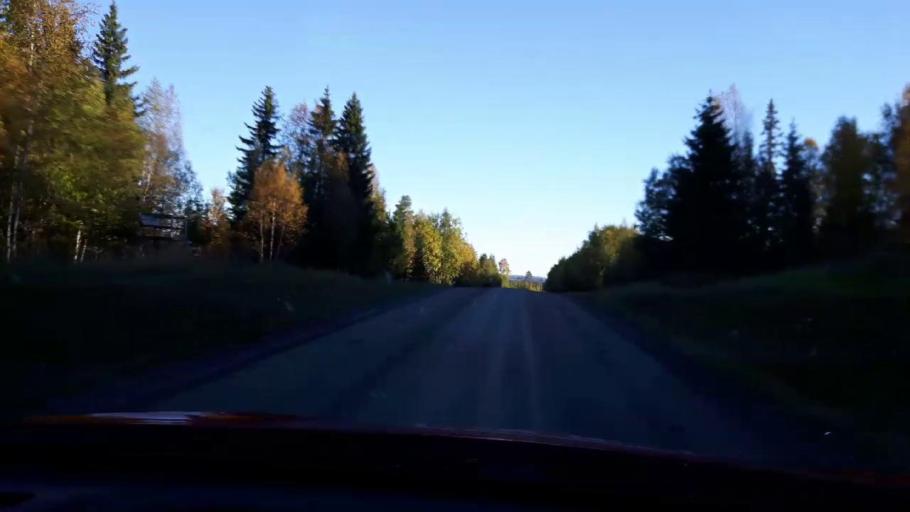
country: SE
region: Jaemtland
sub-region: OEstersunds Kommun
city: Lit
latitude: 63.6630
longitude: 14.7136
